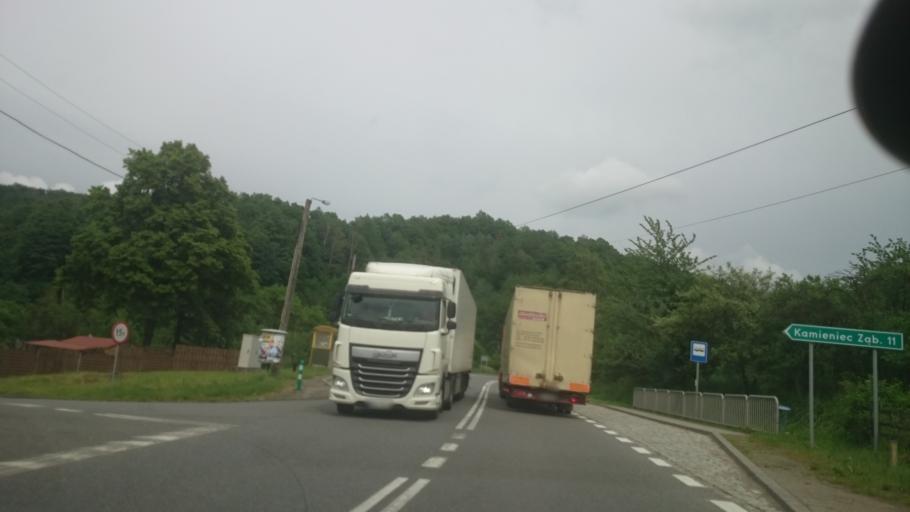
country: PL
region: Lower Silesian Voivodeship
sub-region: Powiat zabkowicki
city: Bardo
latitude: 50.4402
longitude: 16.7911
